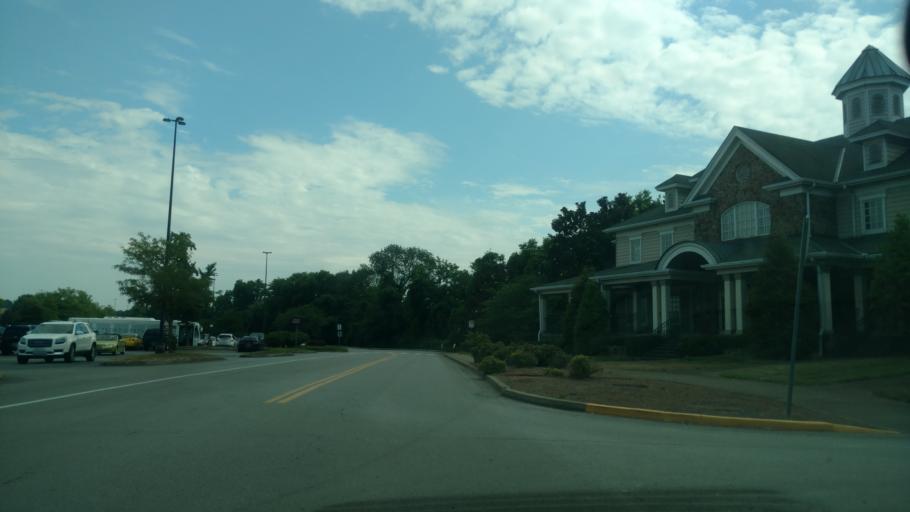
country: US
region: Tennessee
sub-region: Davidson County
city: Lakewood
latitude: 36.2030
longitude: -86.6948
